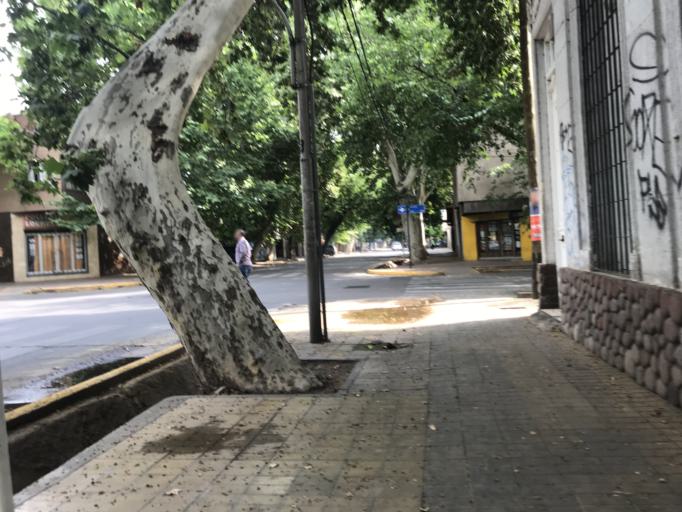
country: AR
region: Mendoza
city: Mendoza
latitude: -32.8819
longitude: -68.8438
